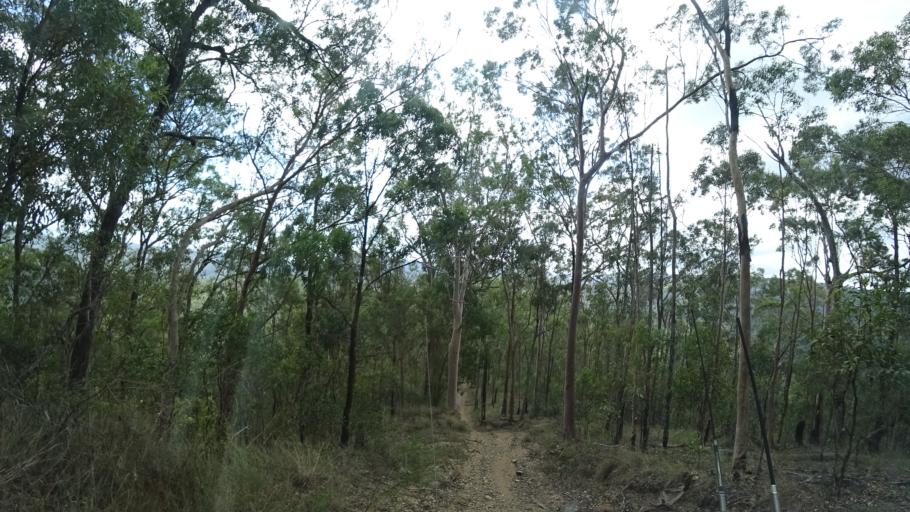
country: AU
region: Queensland
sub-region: Moreton Bay
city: Highvale
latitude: -27.3779
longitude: 152.7378
